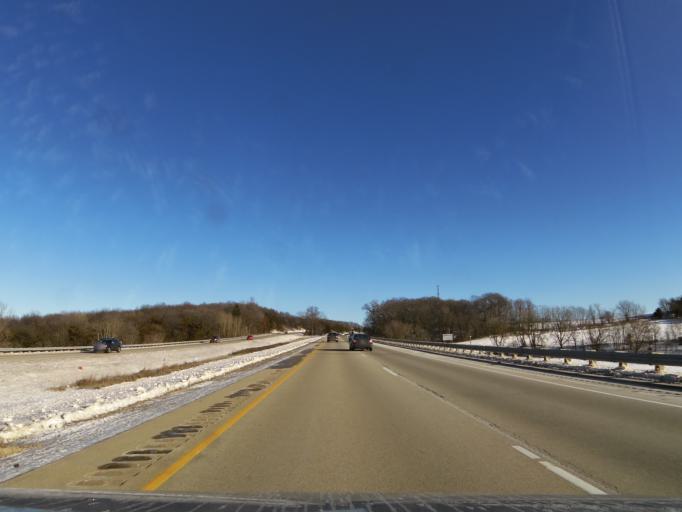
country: US
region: Wisconsin
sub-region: Jefferson County
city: Lake Mills
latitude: 43.1110
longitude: -88.9710
